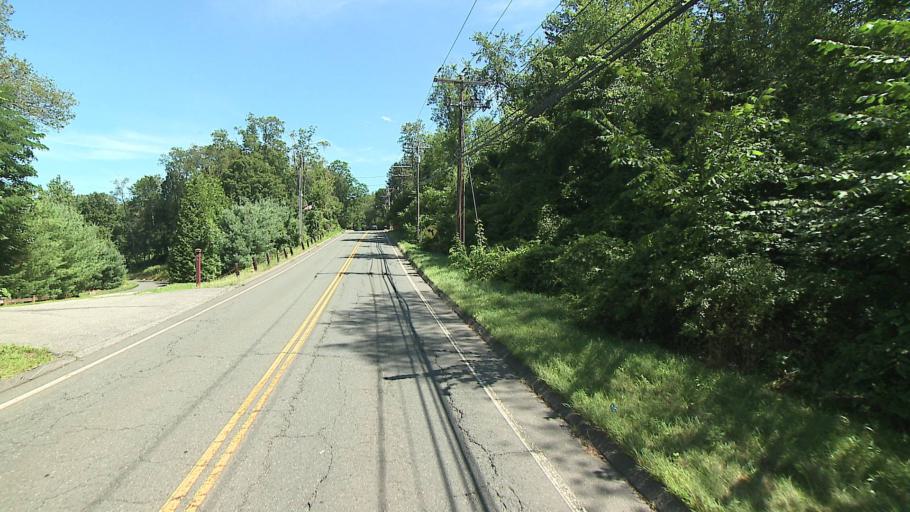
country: US
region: Connecticut
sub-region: Hartford County
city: Collinsville
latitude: 41.8395
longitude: -72.9277
